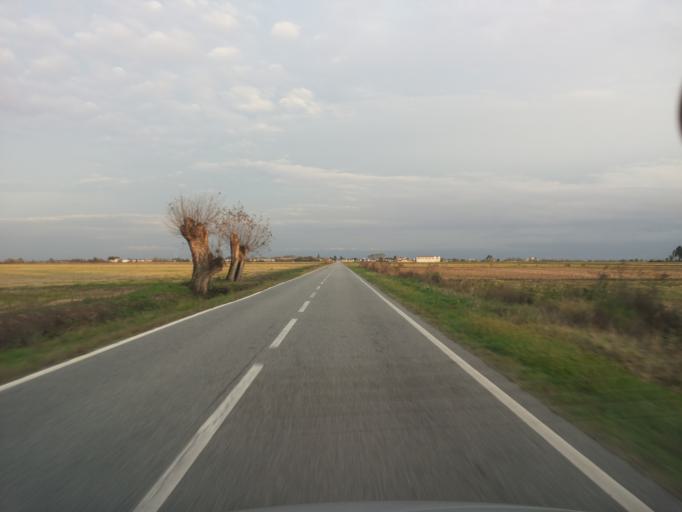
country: IT
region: Piedmont
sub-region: Provincia di Vercelli
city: Pertengo
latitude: 45.2336
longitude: 8.4287
